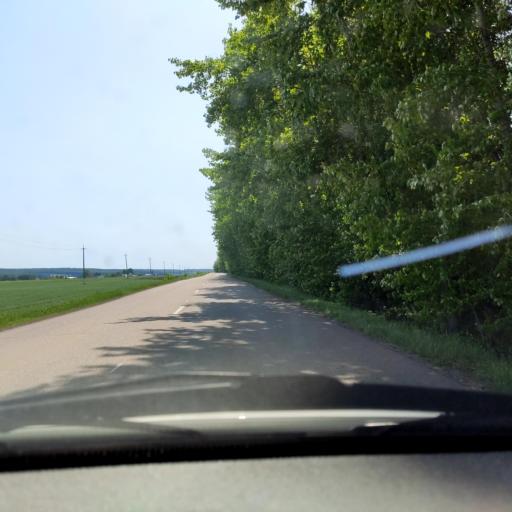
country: RU
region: Bashkortostan
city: Avdon
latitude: 54.5116
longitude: 55.6255
